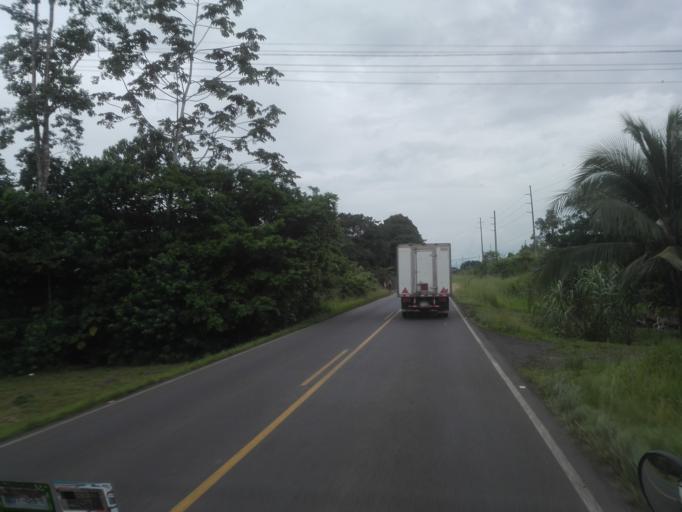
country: CR
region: Heredia
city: La Virgen
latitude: 10.3458
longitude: -83.9560
